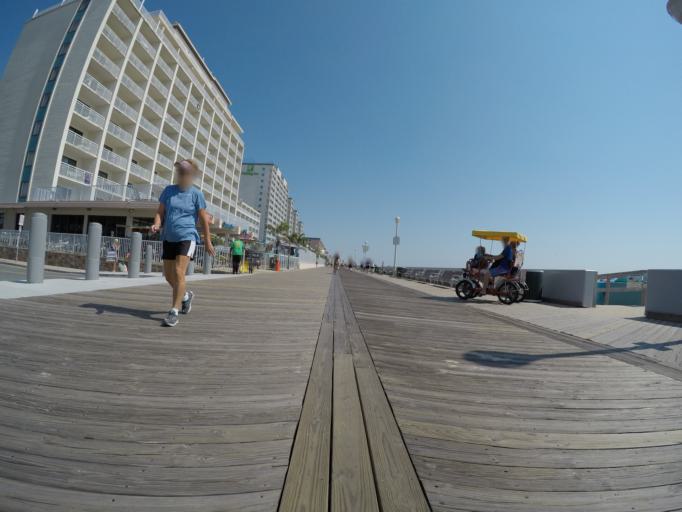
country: US
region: Maryland
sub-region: Worcester County
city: Ocean City
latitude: 38.3456
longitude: -75.0775
